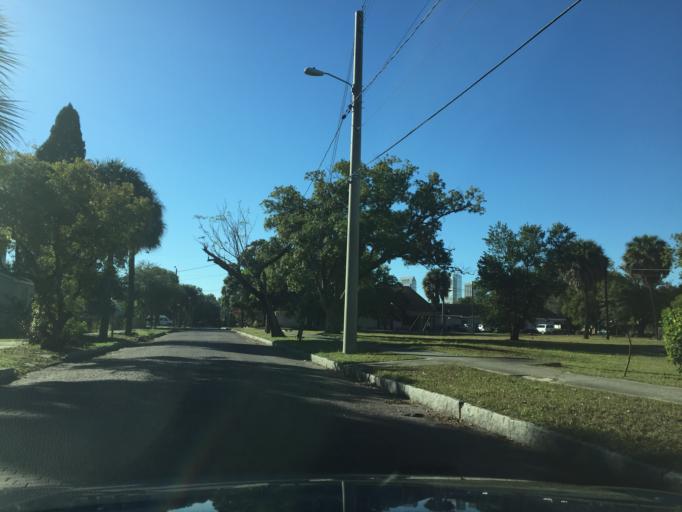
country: US
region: Florida
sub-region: Hillsborough County
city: Tampa
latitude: 27.9613
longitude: -82.4521
